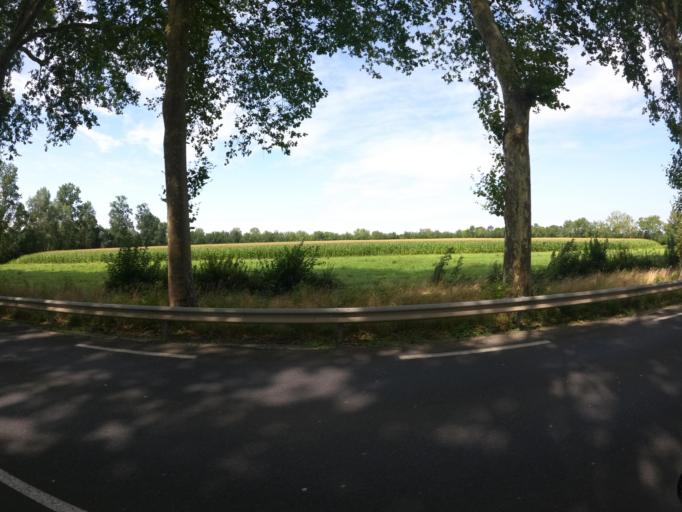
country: FR
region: Poitou-Charentes
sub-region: Departement des Deux-Sevres
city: Frontenay-Rohan-Rohan
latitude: 46.2738
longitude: -0.5261
